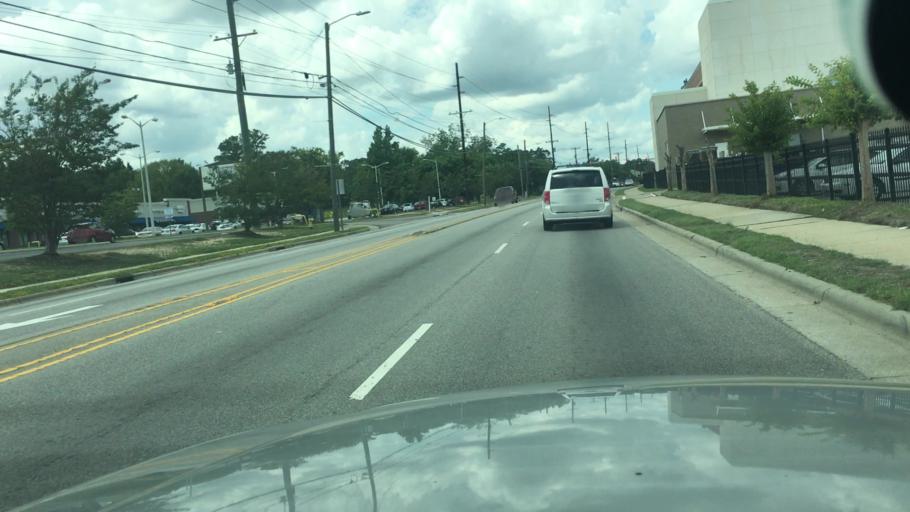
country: US
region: North Carolina
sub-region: Cumberland County
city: Fayetteville
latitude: 35.0699
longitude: -78.8931
